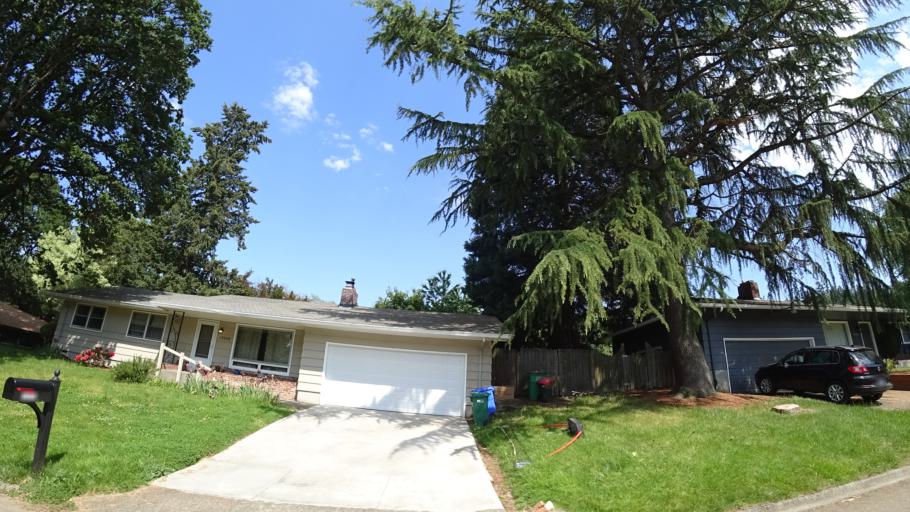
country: US
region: Oregon
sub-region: Washington County
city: Metzger
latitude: 45.4469
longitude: -122.7377
